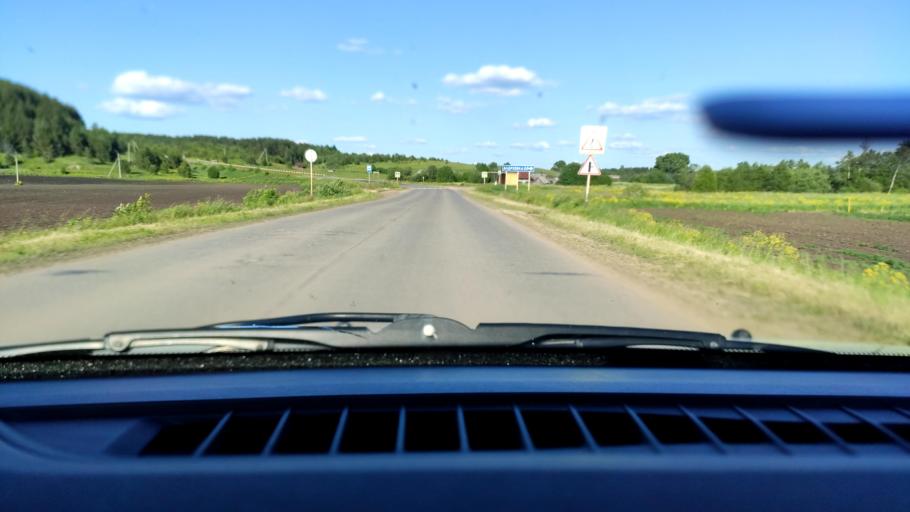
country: RU
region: Perm
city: Uinskoye
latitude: 57.0763
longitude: 56.6033
